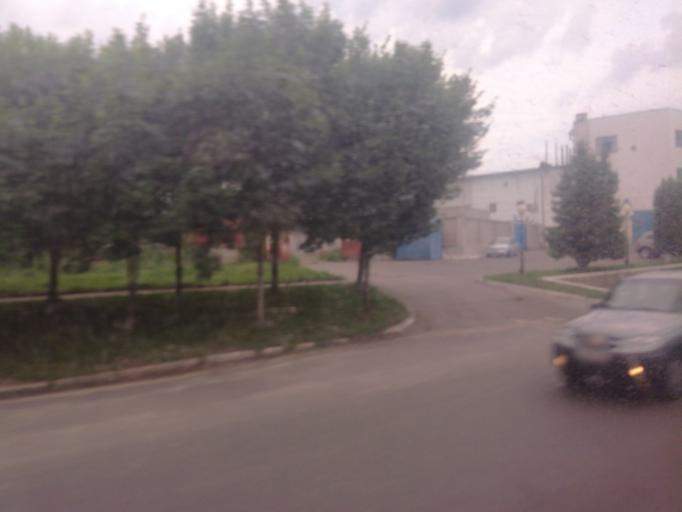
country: RU
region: Kursk
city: Kursk
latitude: 51.7552
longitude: 36.1325
